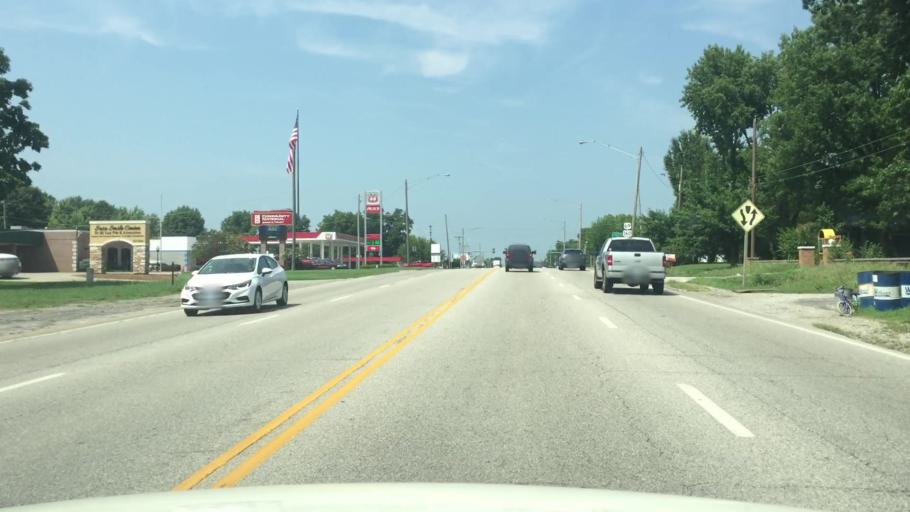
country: US
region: Kansas
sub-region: Crawford County
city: Frontenac
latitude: 37.4526
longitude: -94.7051
